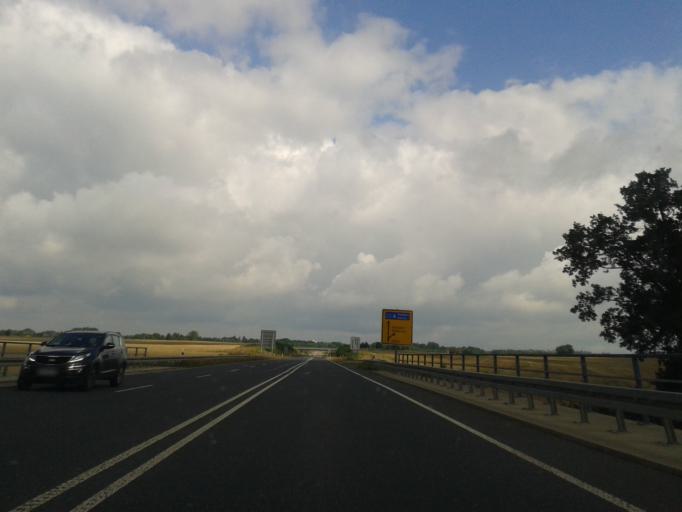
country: DE
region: Saxony
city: Radeberg
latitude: 51.1074
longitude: 13.9371
